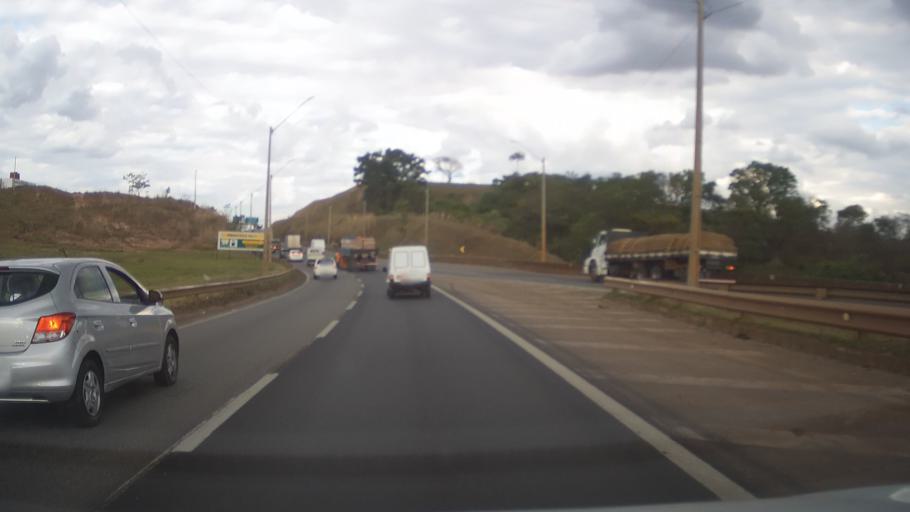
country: BR
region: Minas Gerais
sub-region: Betim
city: Betim
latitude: -19.9611
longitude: -44.1550
